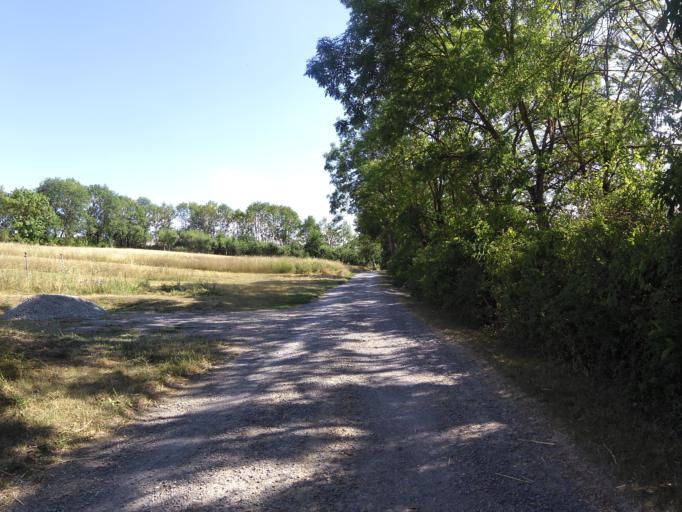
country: DE
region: Bavaria
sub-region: Regierungsbezirk Unterfranken
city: Rimpar
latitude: 49.8337
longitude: 9.9592
